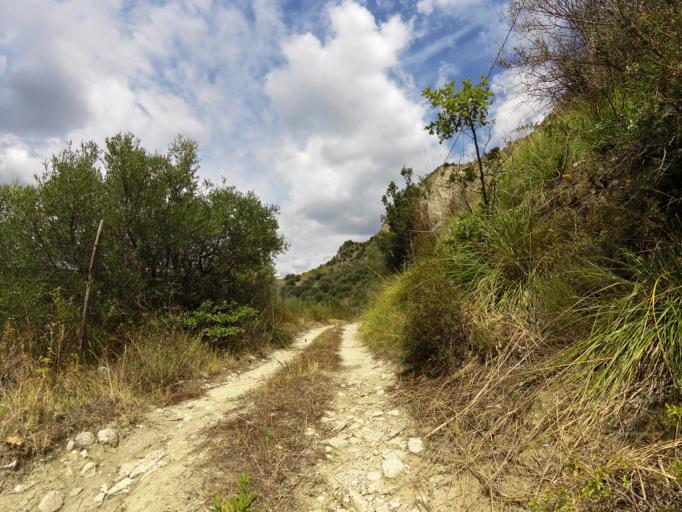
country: IT
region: Calabria
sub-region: Provincia di Reggio Calabria
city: Camini
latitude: 38.4516
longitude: 16.4748
